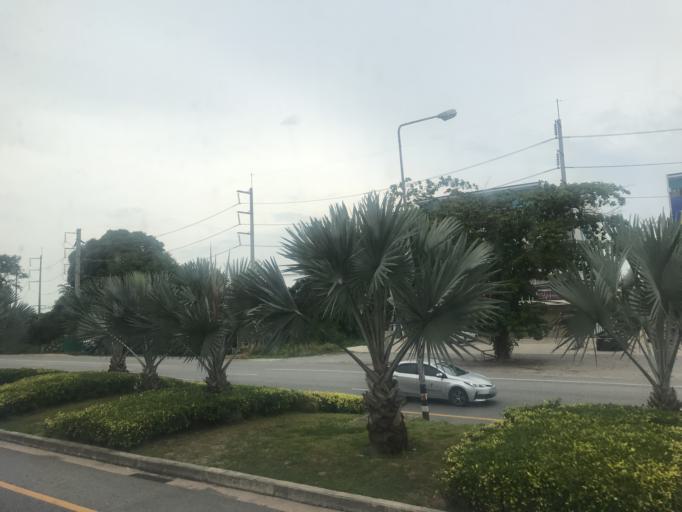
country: TH
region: Chon Buri
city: Bang Lamung
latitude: 13.0098
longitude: 100.9309
